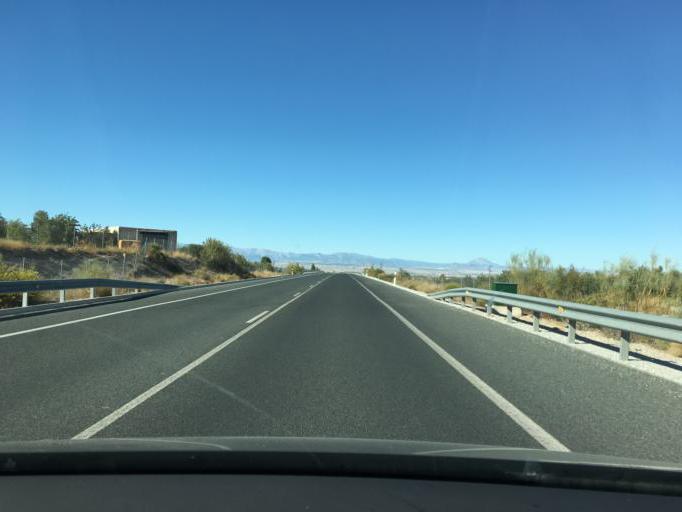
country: ES
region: Andalusia
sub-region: Provincia de Granada
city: Caniles
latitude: 37.4627
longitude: -2.7372
